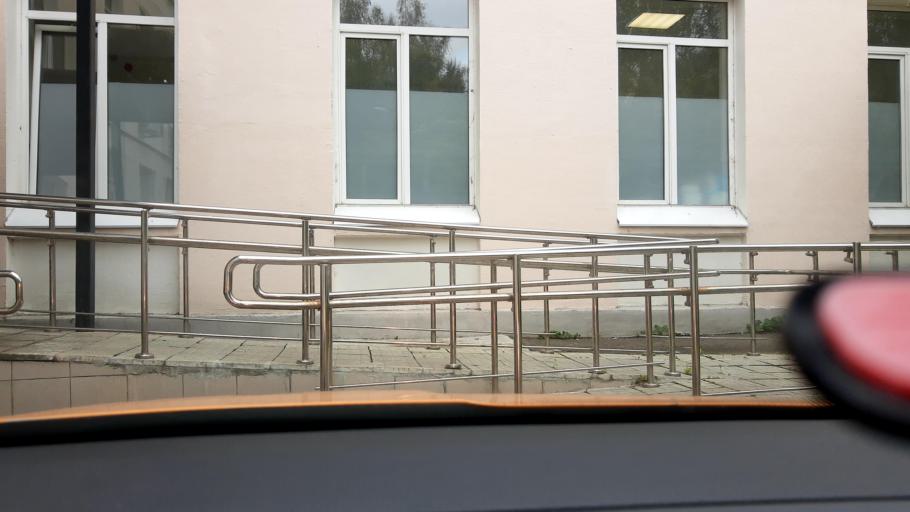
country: RU
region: Moscow
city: Pokrovskoye-Streshnevo
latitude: 55.8160
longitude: 37.4541
